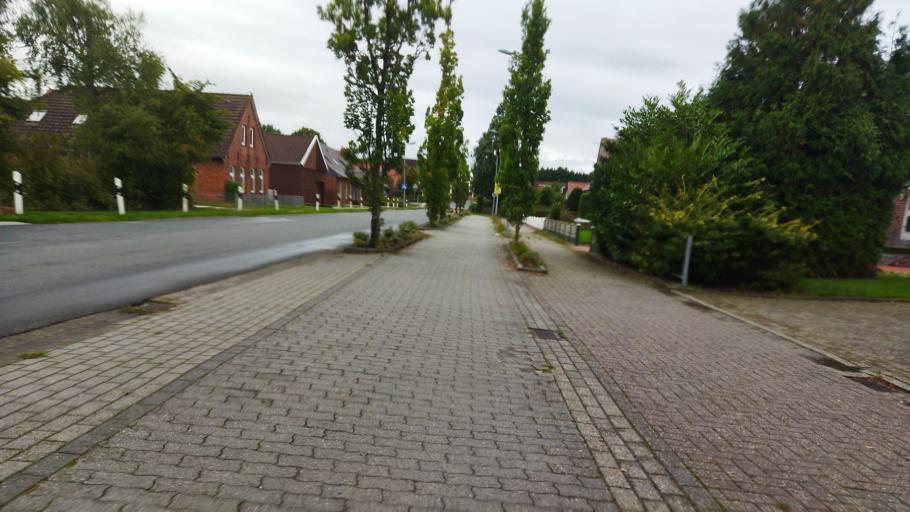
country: DE
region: Lower Saxony
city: Hinte
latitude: 53.4173
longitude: 7.1922
